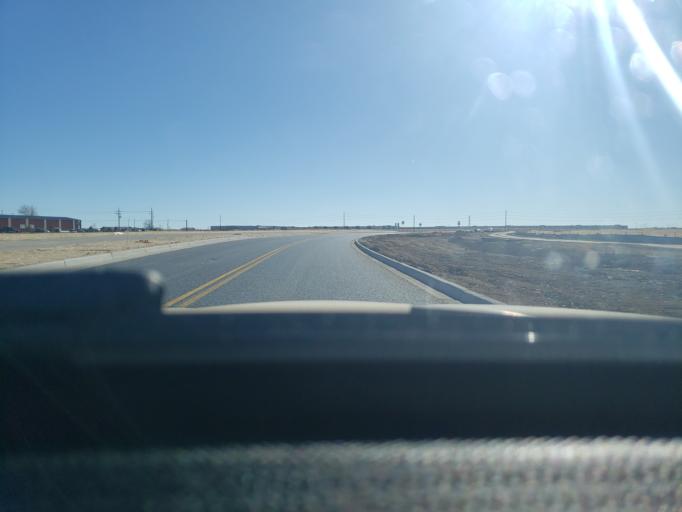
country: US
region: Colorado
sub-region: Adams County
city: Aurora
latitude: 39.7566
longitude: -104.7131
